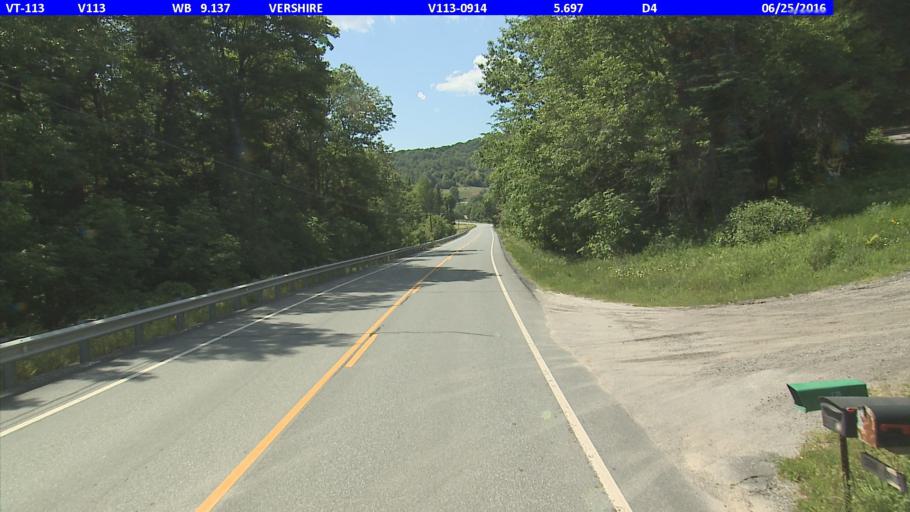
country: US
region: New Hampshire
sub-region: Grafton County
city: Orford
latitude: 43.9605
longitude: -72.2852
